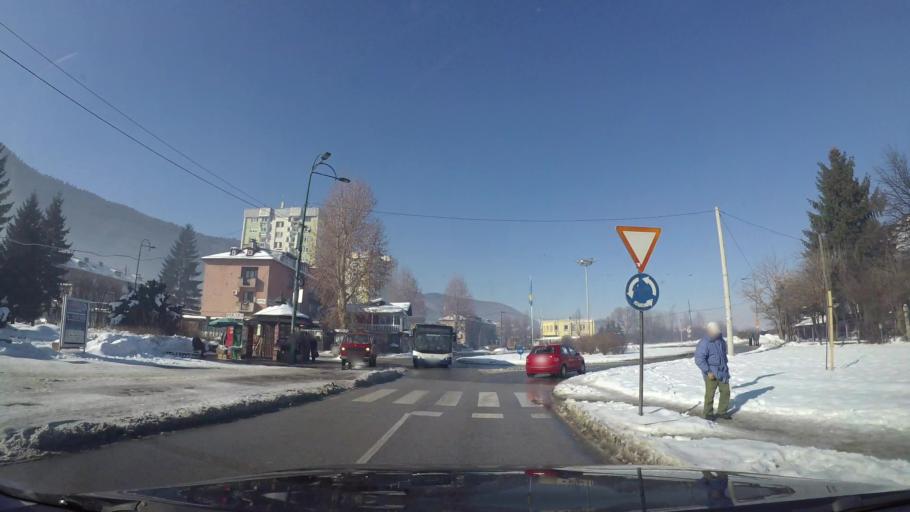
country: BA
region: Federation of Bosnia and Herzegovina
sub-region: Kanton Sarajevo
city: Sarajevo
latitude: 43.7988
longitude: 18.3138
